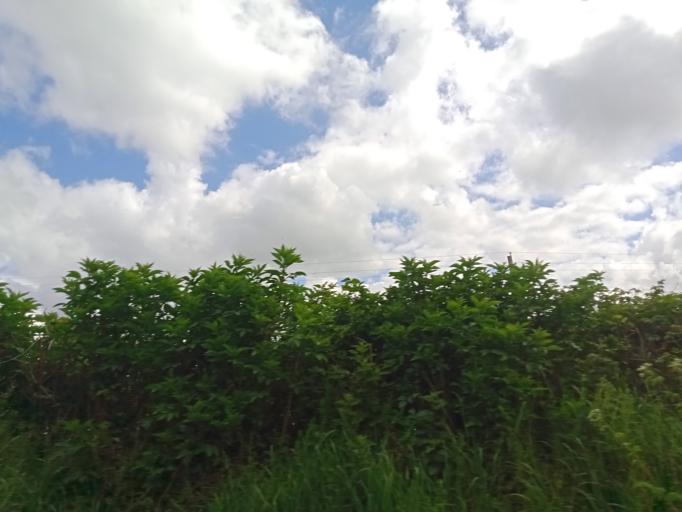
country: IE
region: Munster
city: Thurles
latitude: 52.6715
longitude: -7.6753
